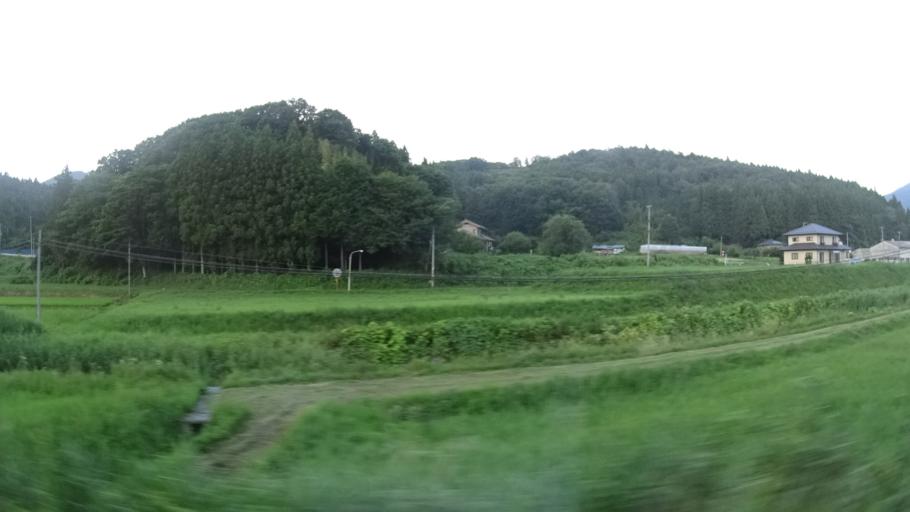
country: JP
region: Fukushima
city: Funehikimachi-funehiki
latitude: 37.3349
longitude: 140.6568
